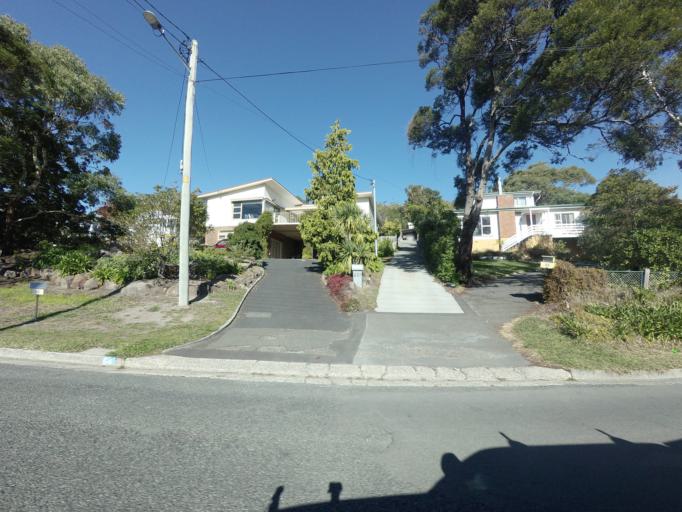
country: AU
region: Tasmania
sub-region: Clarence
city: Lindisfarne
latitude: -42.8414
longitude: 147.3435
